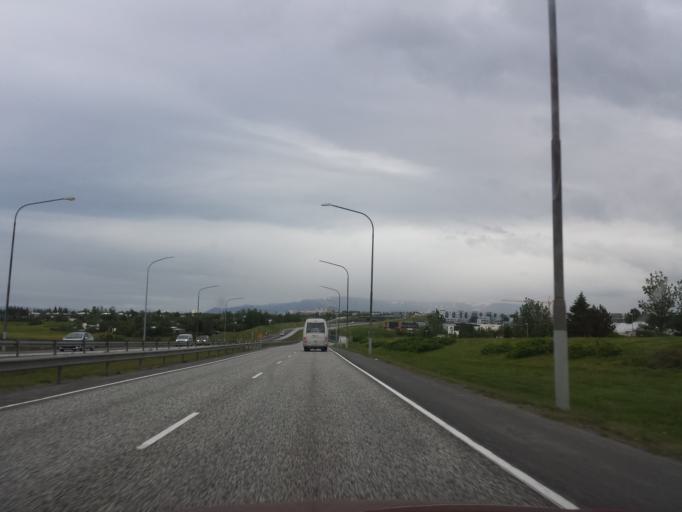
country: IS
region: Capital Region
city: Gardabaer
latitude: 64.0932
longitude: -21.9246
